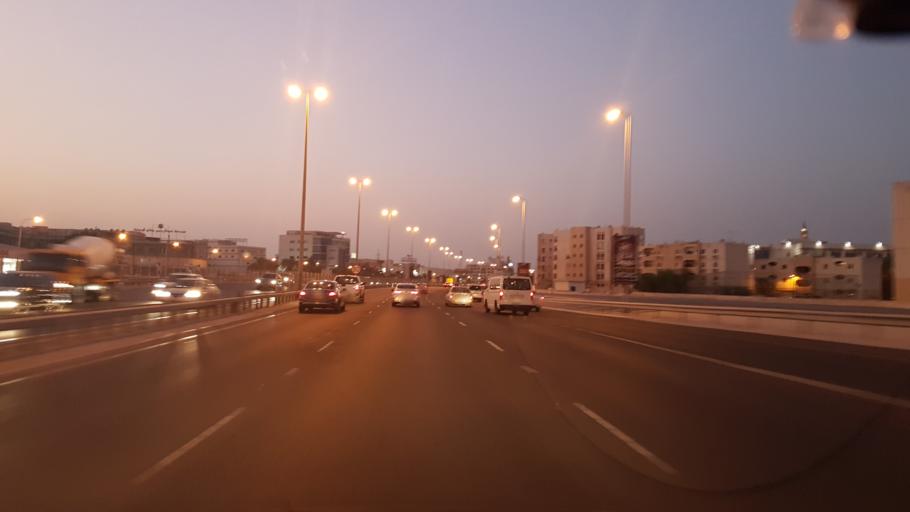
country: BH
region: Northern
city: Madinat `Isa
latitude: 26.1783
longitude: 50.5394
